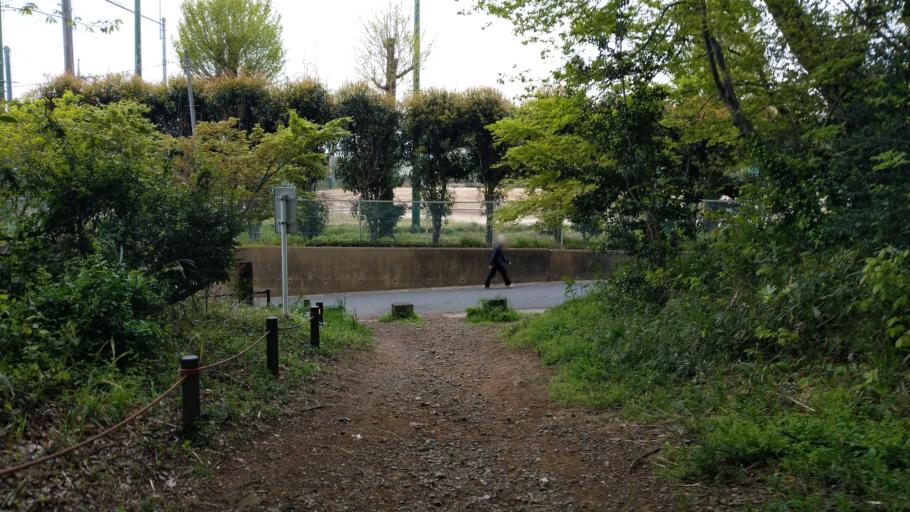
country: JP
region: Saitama
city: Ageoshimo
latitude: 35.9436
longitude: 139.6007
